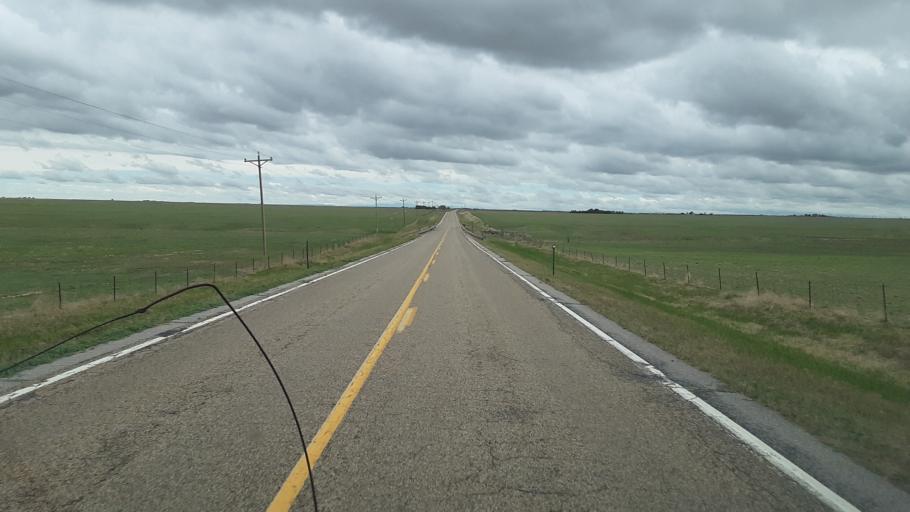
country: US
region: Colorado
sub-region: El Paso County
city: Ellicott
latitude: 38.8398
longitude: -103.9506
